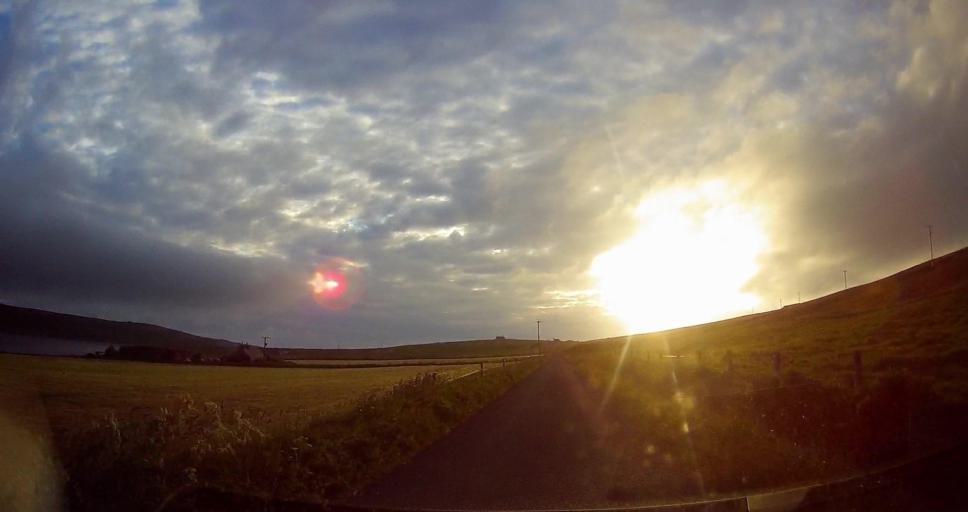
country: GB
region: Scotland
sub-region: Orkney Islands
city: Stromness
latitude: 59.1178
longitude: -3.2648
